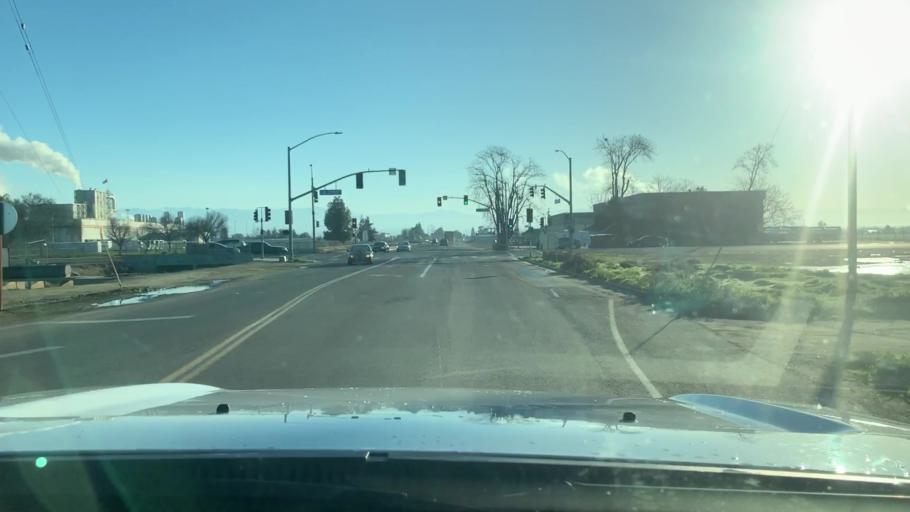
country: US
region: California
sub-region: Tulare County
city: Tulare
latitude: 36.1821
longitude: -119.3412
